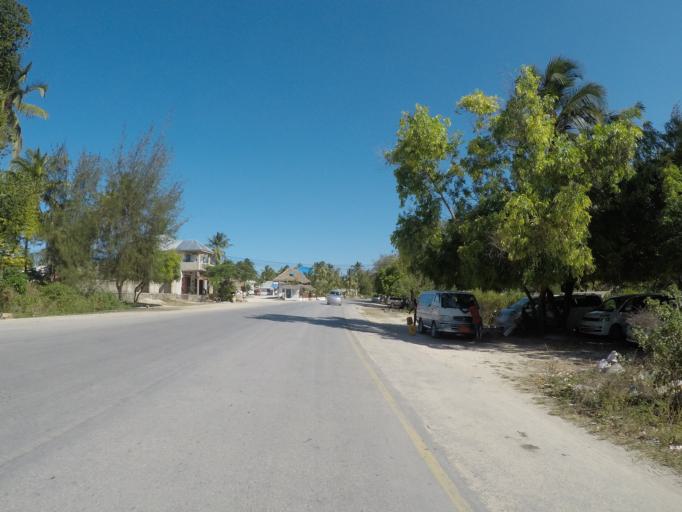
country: TZ
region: Zanzibar Central/South
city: Nganane
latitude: -6.2682
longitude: 39.5323
